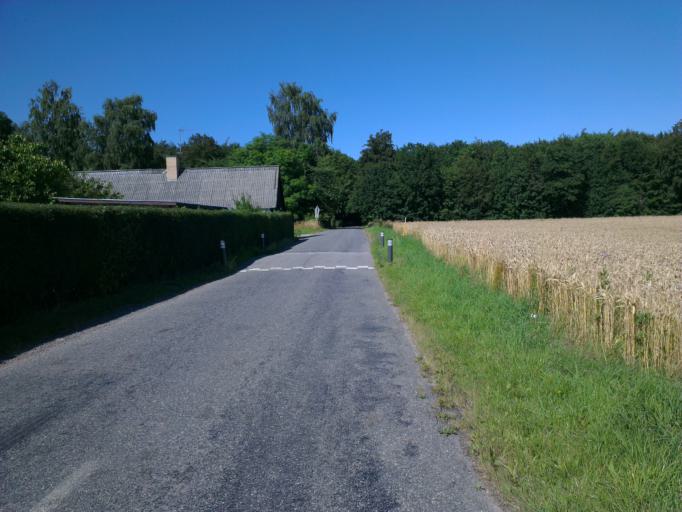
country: DK
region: Capital Region
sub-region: Frederikssund Kommune
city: Skibby
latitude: 55.7159
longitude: 11.9502
